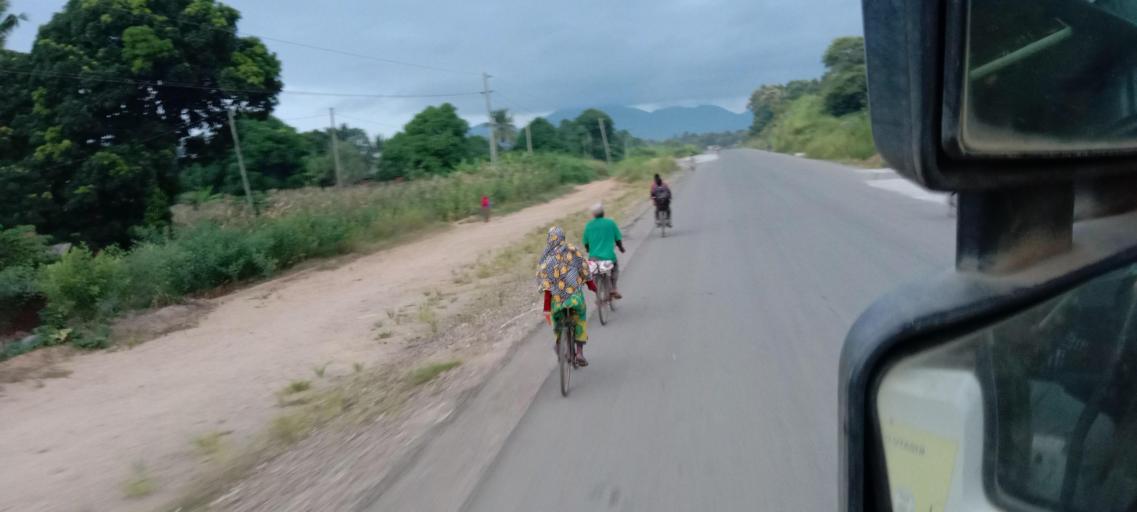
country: TZ
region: Morogoro
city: Ifakara
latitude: -7.9588
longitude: 36.8529
